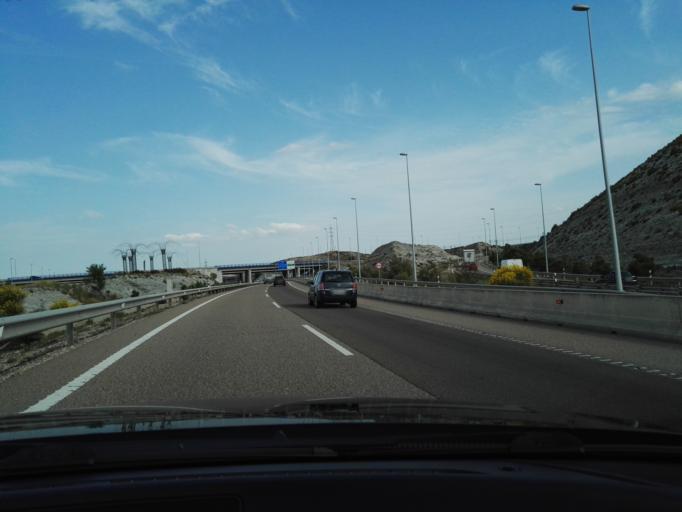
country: ES
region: Aragon
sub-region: Provincia de Zaragoza
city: Montecanal
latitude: 41.6158
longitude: -0.9353
